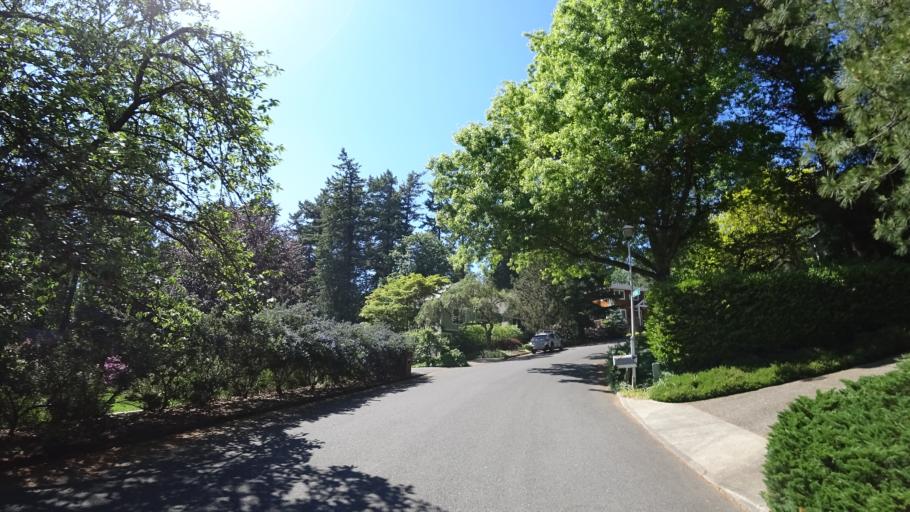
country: US
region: Oregon
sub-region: Washington County
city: West Slope
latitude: 45.4962
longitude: -122.7223
